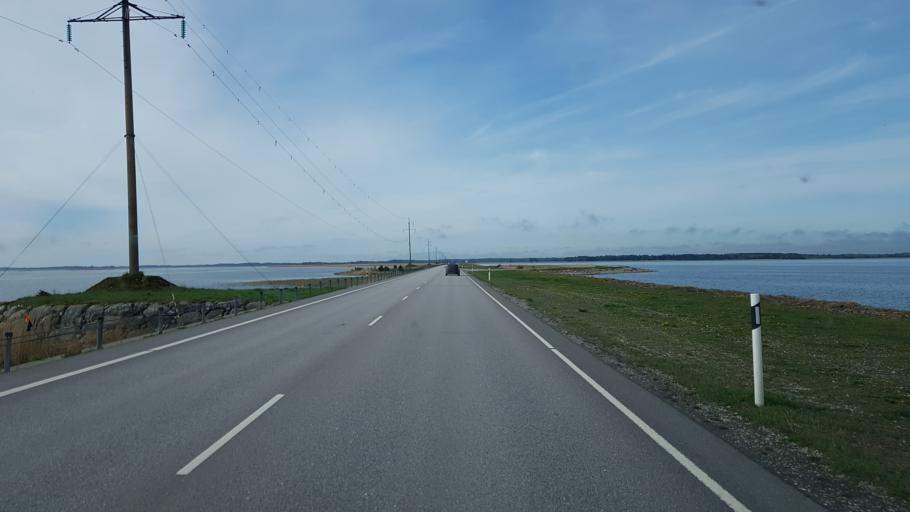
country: EE
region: Saare
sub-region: Orissaare vald
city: Orissaare
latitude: 58.5656
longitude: 23.1603
